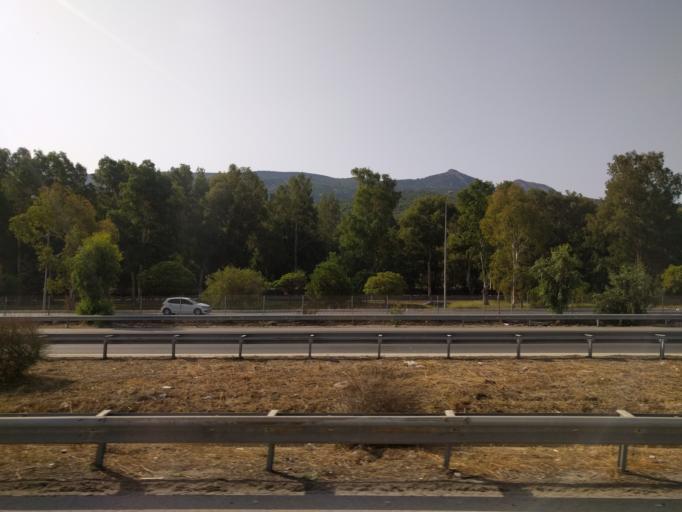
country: TR
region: Izmir
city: Karsiyaka
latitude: 38.3953
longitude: 26.9753
